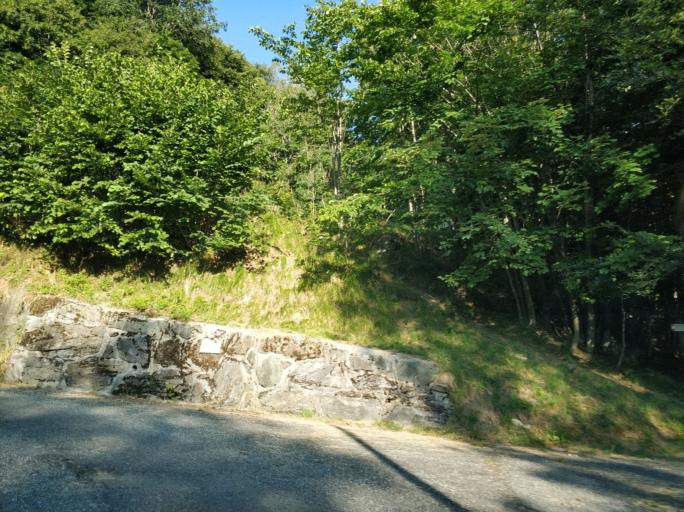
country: IT
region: Piedmont
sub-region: Provincia di Torino
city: Usseglio
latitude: 45.2334
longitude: 7.2075
